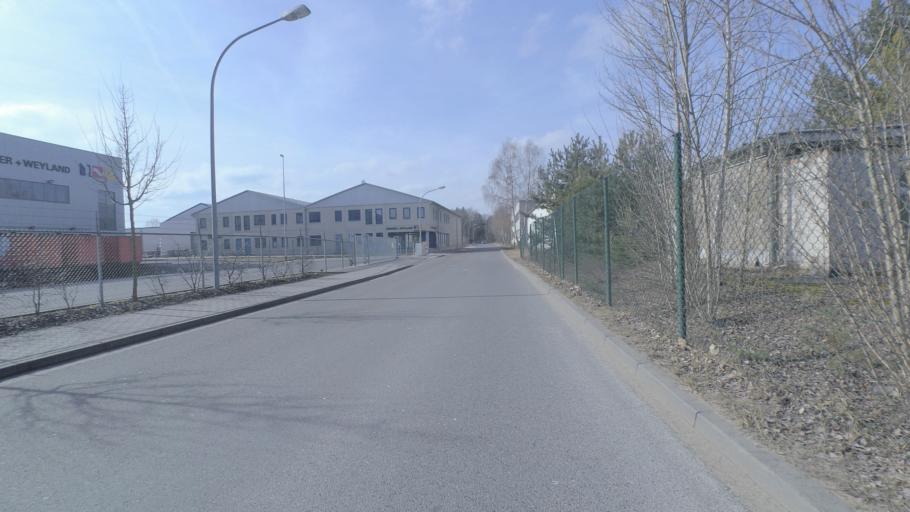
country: DE
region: Brandenburg
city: Ludwigsfelde
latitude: 52.3043
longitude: 13.2763
